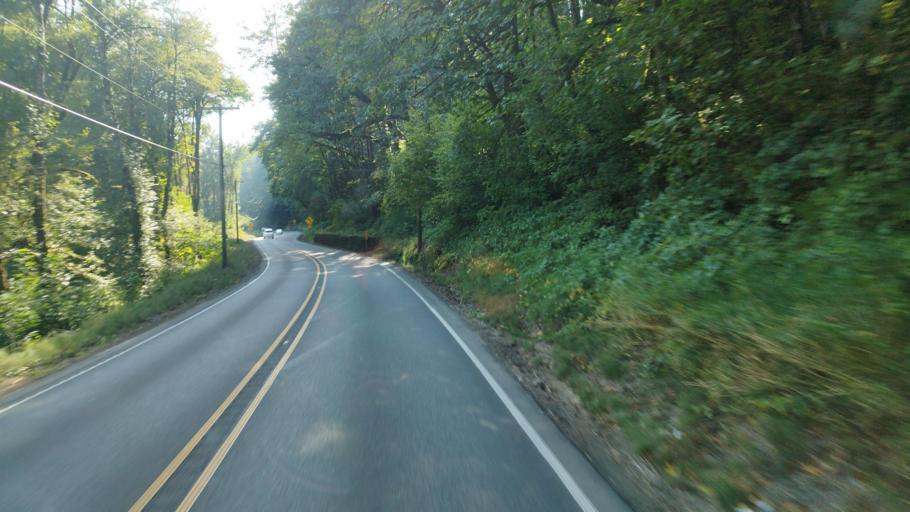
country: US
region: Oregon
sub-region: Washington County
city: Bethany
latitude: 45.6482
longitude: -122.8555
